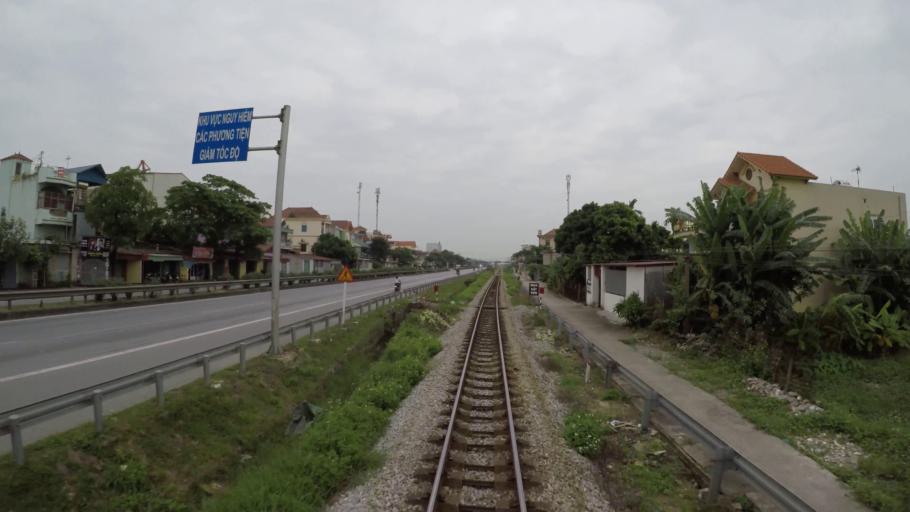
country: VN
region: Hai Duong
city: Phu Thai
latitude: 20.9426
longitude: 106.5444
